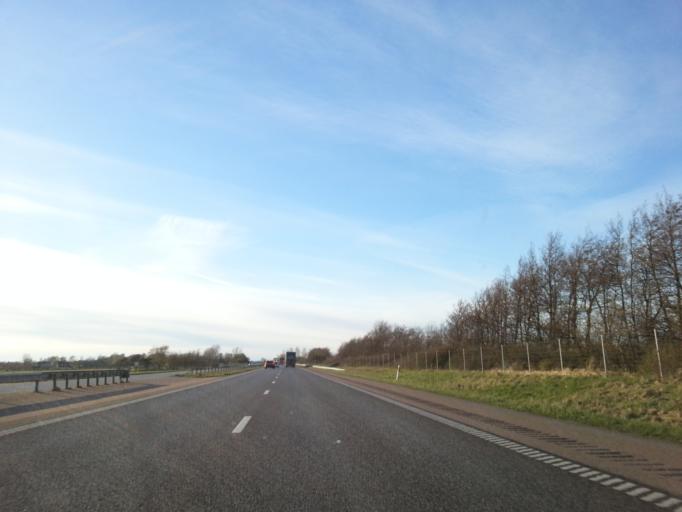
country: SE
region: Halland
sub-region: Halmstads Kommun
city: Paarp
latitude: 56.5914
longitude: 12.9394
